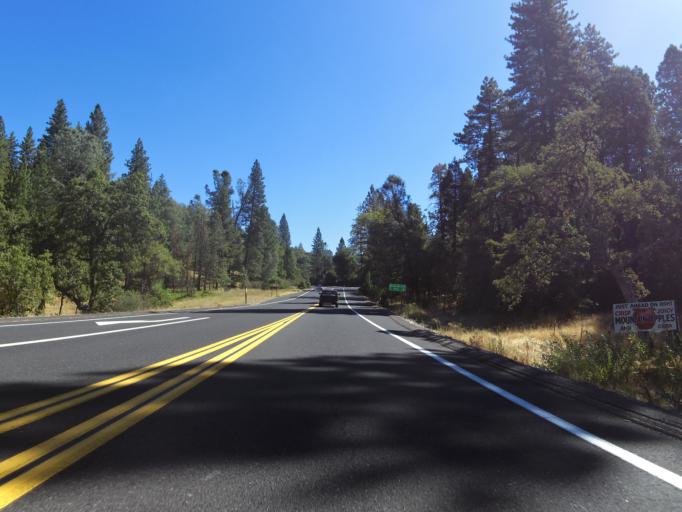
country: US
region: California
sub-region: Calaveras County
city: Forest Meadows
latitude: 38.1780
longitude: -120.3851
